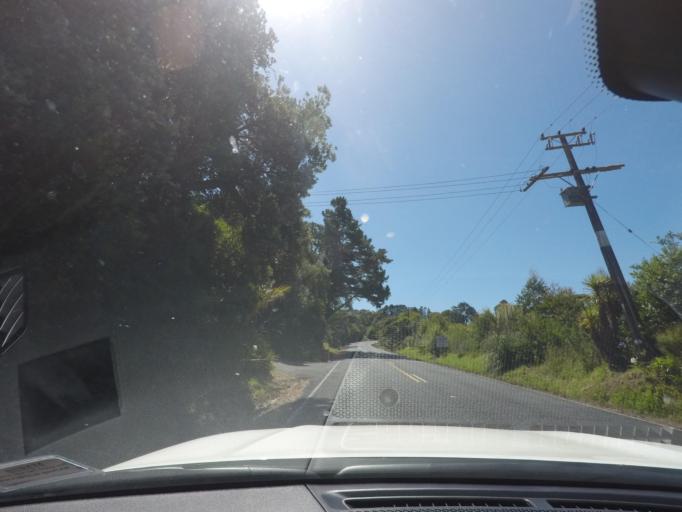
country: NZ
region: Auckland
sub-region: Auckland
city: Parakai
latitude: -36.6141
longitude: 174.3408
